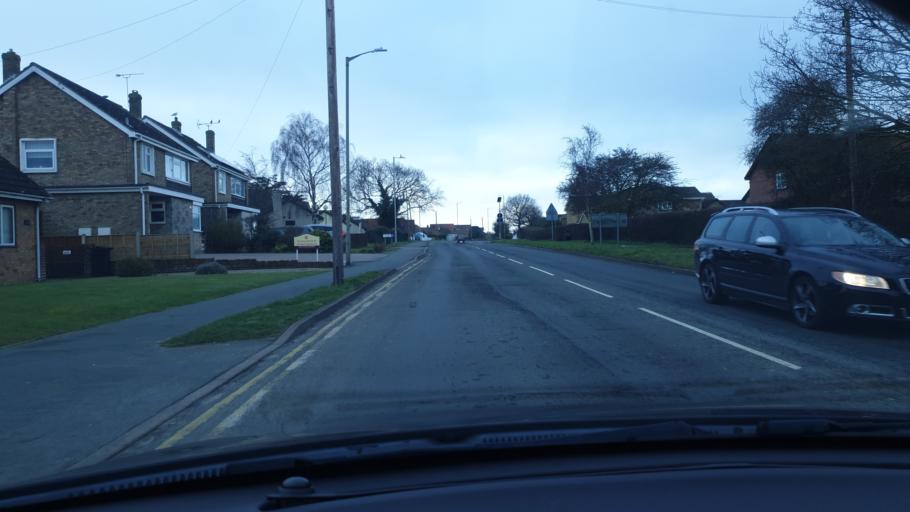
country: GB
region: England
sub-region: Essex
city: Frinton-on-Sea
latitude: 51.8434
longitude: 1.2477
